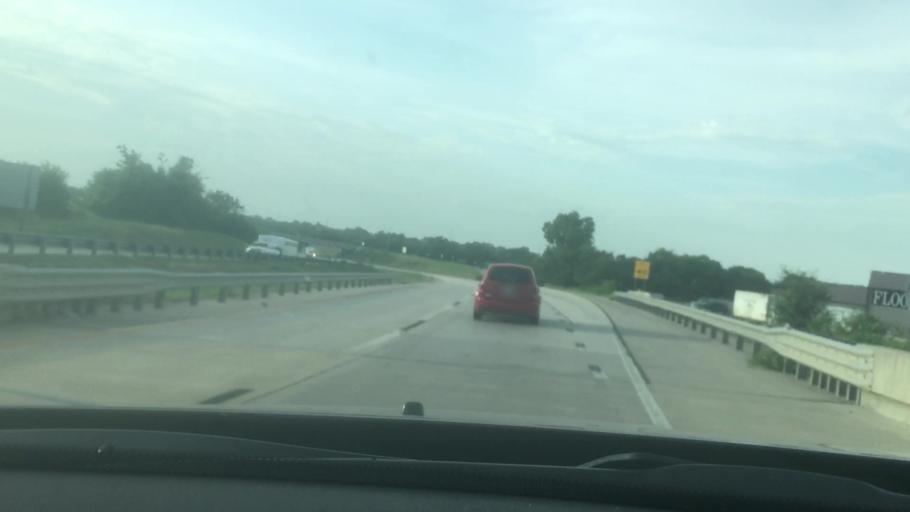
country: US
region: Oklahoma
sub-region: Pontotoc County
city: Ada
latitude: 34.7672
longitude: -96.7047
